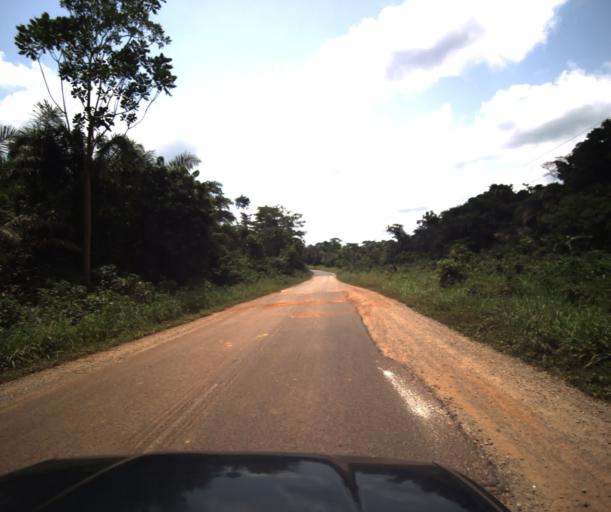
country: CM
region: Centre
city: Eseka
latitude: 3.8106
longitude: 10.8056
